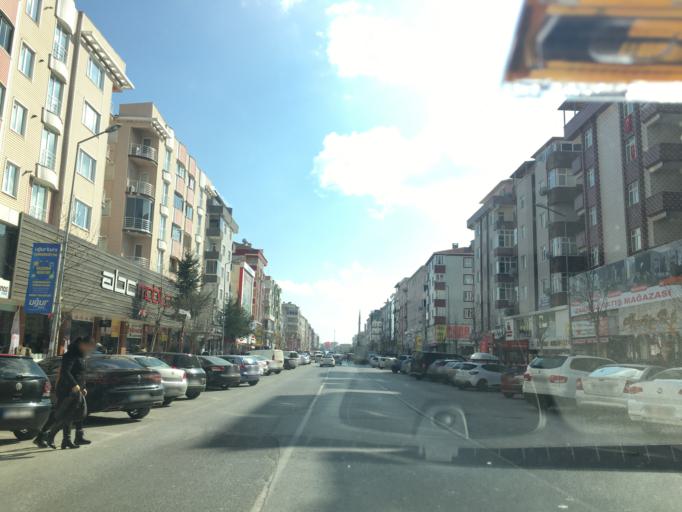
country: TR
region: Tekirdag
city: Cerkezkoey
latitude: 41.2921
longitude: 27.9982
